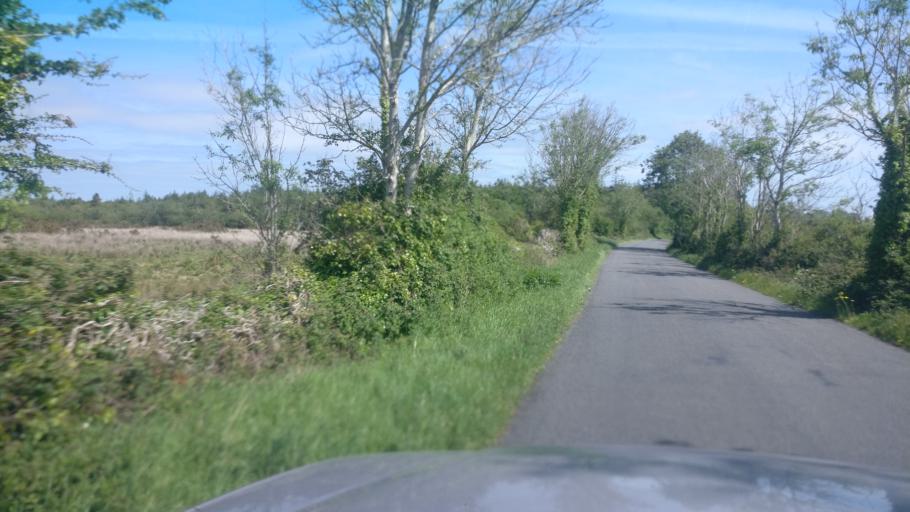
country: IE
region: Connaught
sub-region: County Galway
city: Gort
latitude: 53.1252
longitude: -8.7818
